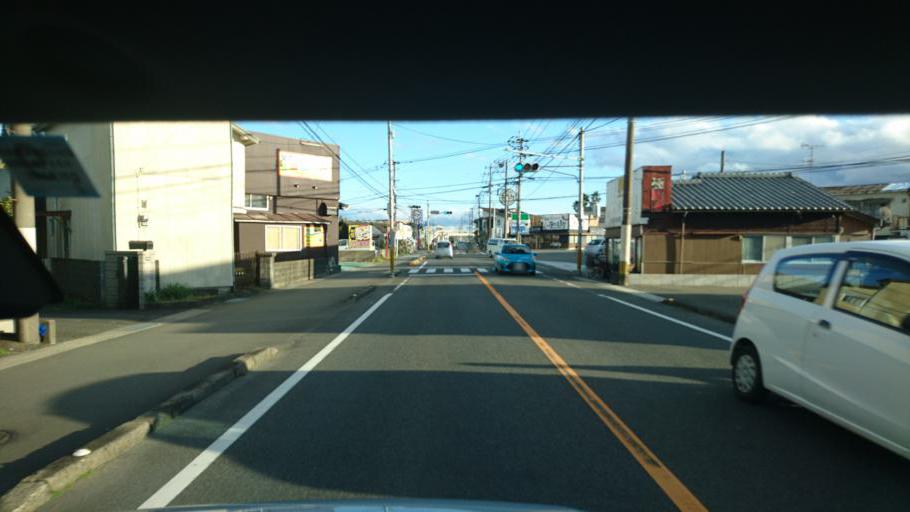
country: JP
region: Miyazaki
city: Miyazaki-shi
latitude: 31.8873
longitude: 131.4241
